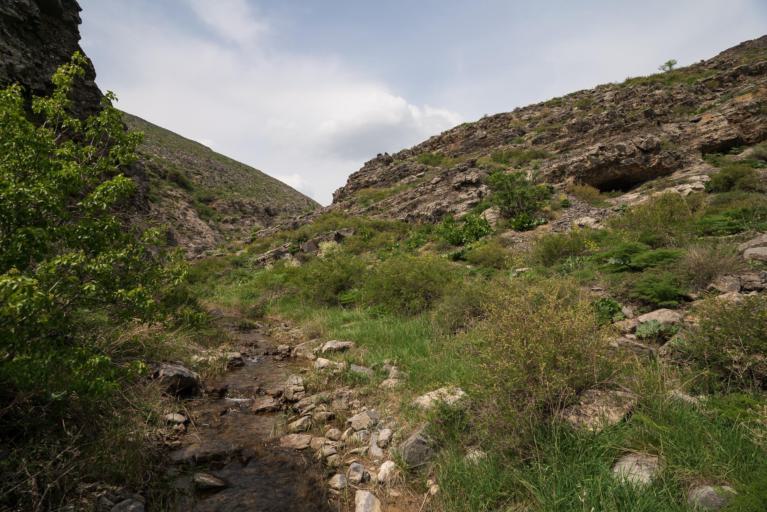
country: KZ
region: Ongtustik Qazaqstan
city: Ashchysay
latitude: 43.5358
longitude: 68.8412
